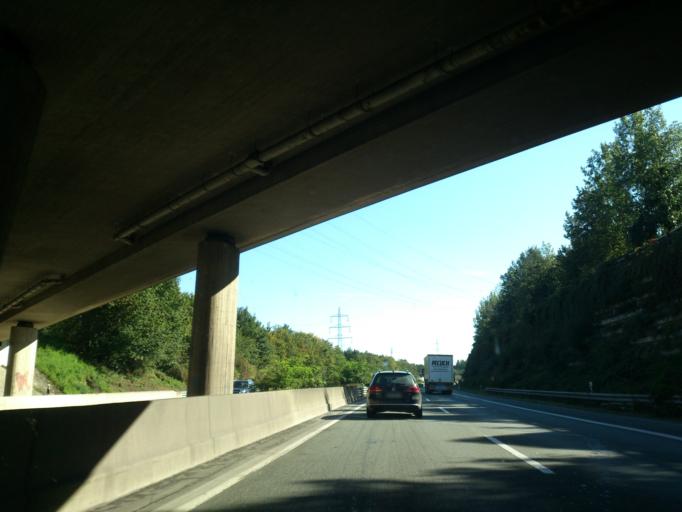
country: DE
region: North Rhine-Westphalia
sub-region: Regierungsbezirk Detmold
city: Oerlinghausen
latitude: 51.9018
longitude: 8.6306
